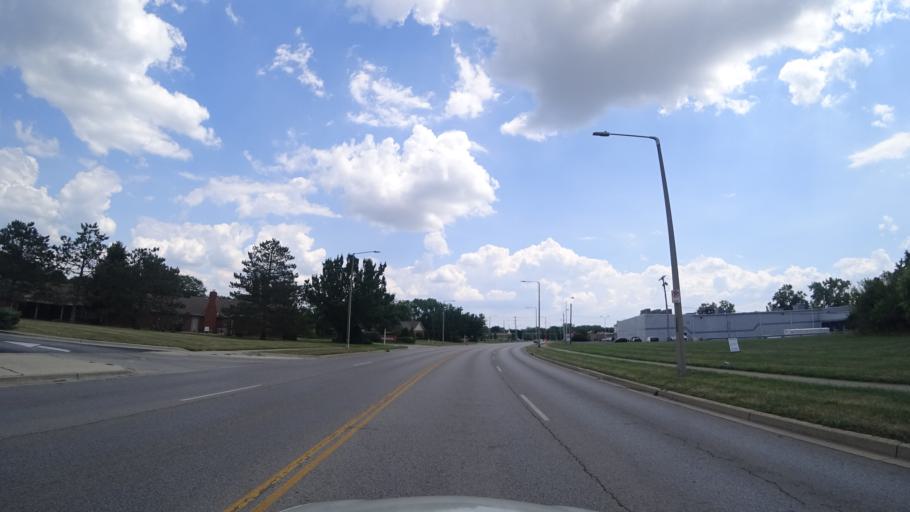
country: US
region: Ohio
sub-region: Butler County
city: Hamilton
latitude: 39.4262
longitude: -84.5873
